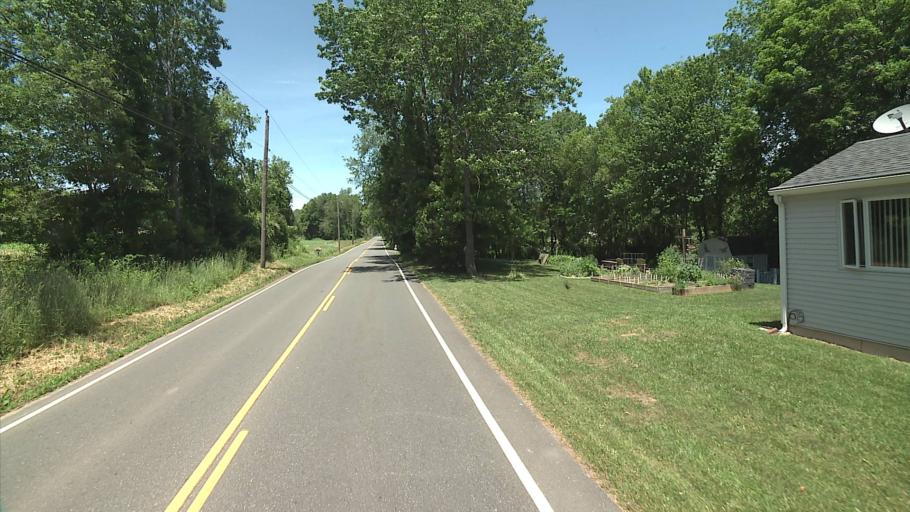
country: US
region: Rhode Island
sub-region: Washington County
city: Ashaway
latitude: 41.4433
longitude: -71.8023
